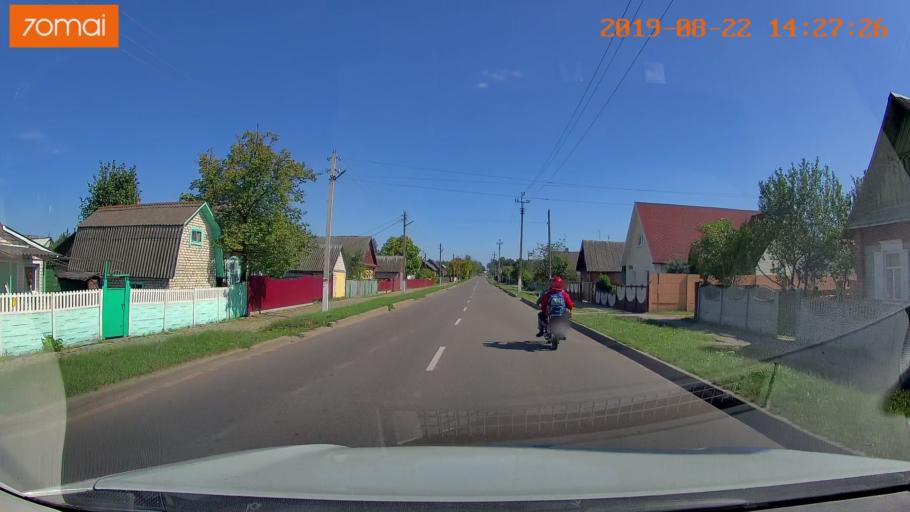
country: BY
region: Mogilev
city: Asipovichy
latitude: 53.2969
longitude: 28.6262
